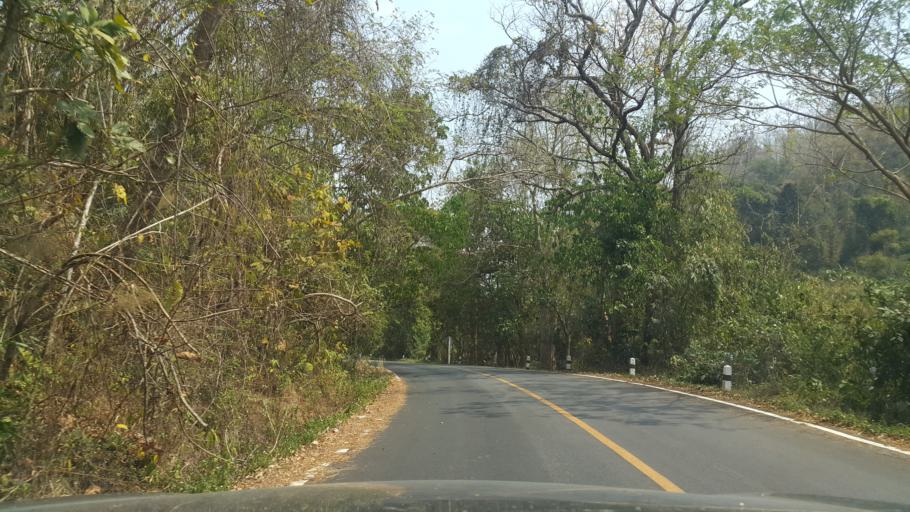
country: TH
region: Lamphun
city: Thung Hua Chang
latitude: 17.9057
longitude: 99.1198
